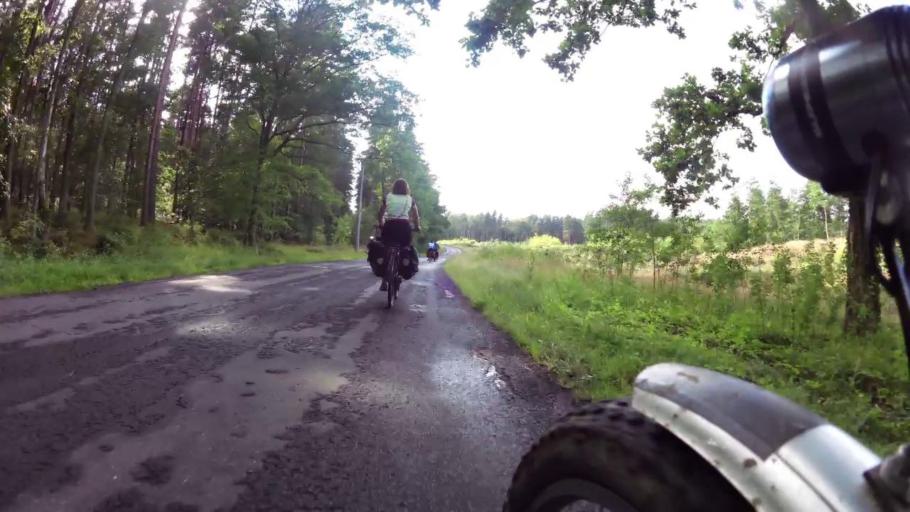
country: PL
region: West Pomeranian Voivodeship
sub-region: Powiat gryfinski
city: Gryfino
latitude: 53.2307
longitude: 14.5442
